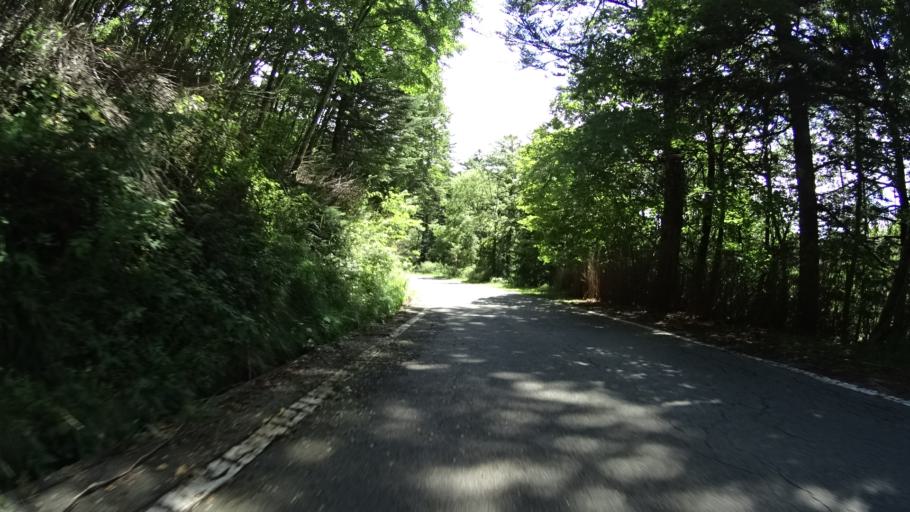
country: JP
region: Yamanashi
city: Enzan
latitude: 35.7322
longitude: 138.8424
